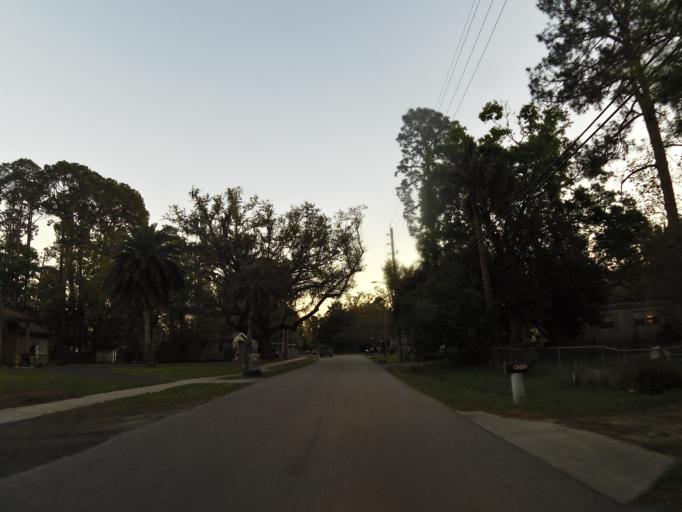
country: US
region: Florida
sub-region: Duval County
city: Jacksonville
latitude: 30.2765
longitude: -81.6310
